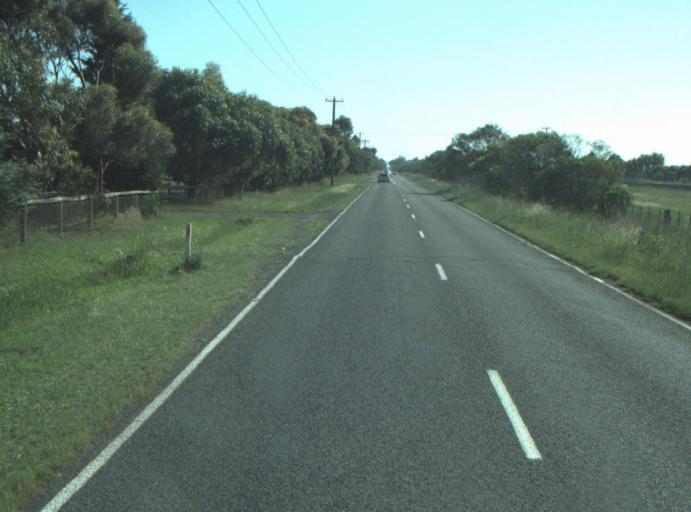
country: AU
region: Victoria
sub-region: Greater Geelong
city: Lara
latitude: -38.0133
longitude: 144.4243
